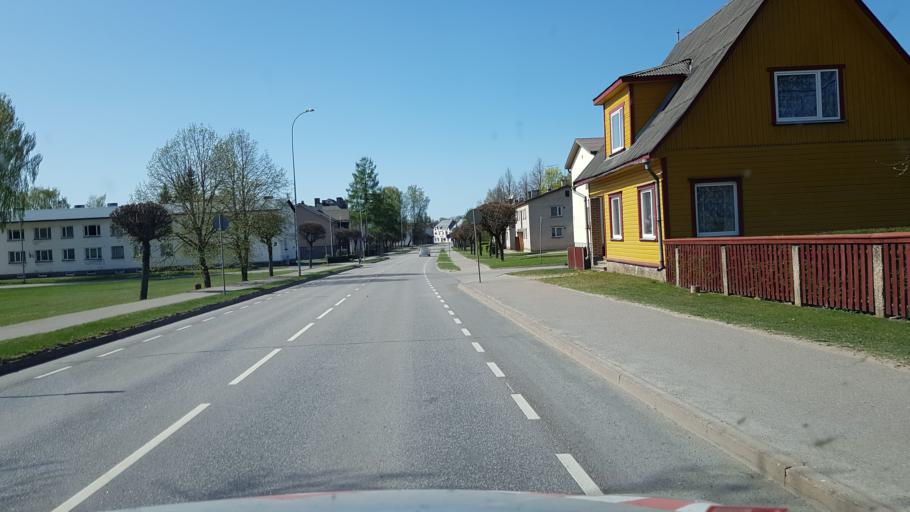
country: EE
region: Valgamaa
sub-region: Torva linn
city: Torva
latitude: 58.0004
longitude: 25.9281
